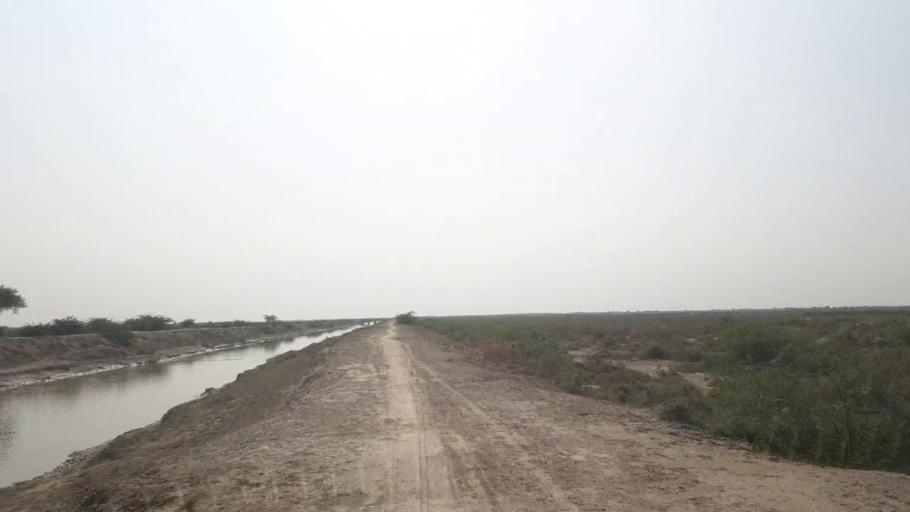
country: PK
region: Sindh
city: Kadhan
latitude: 24.3851
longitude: 68.8997
